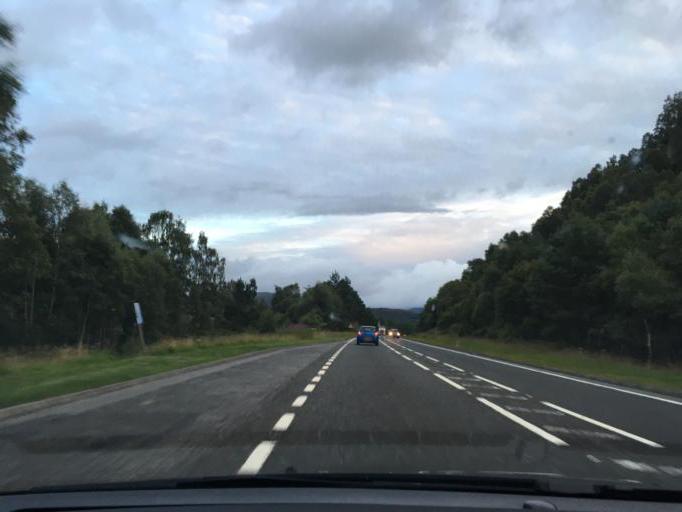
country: GB
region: Scotland
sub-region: Highland
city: Aviemore
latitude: 57.1841
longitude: -3.8353
